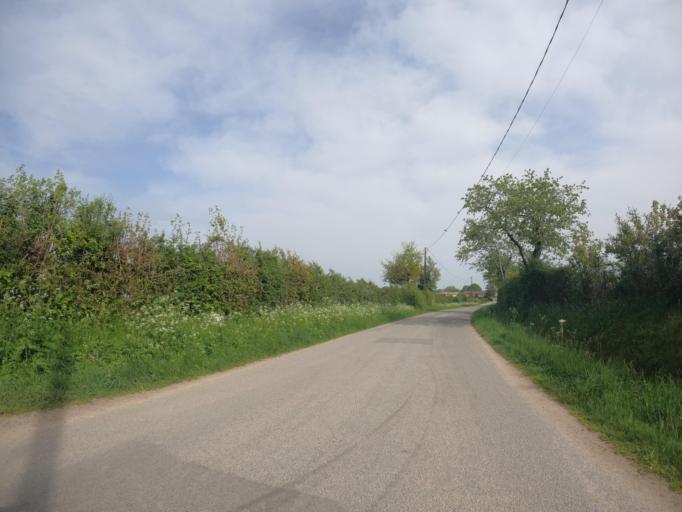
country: FR
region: Poitou-Charentes
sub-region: Departement des Deux-Sevres
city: La Chapelle-Saint-Laurent
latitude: 46.7035
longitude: -0.5215
